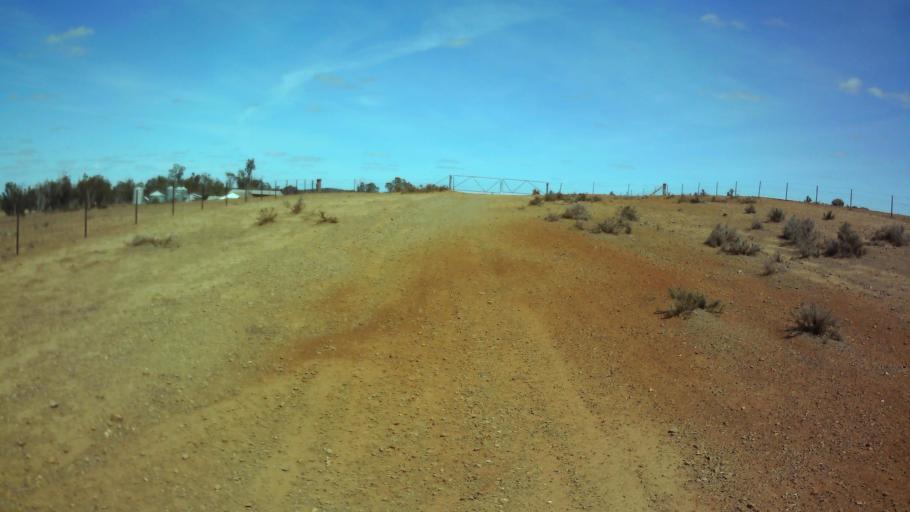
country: AU
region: New South Wales
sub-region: Forbes
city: Forbes
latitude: -33.7173
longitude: 147.8149
